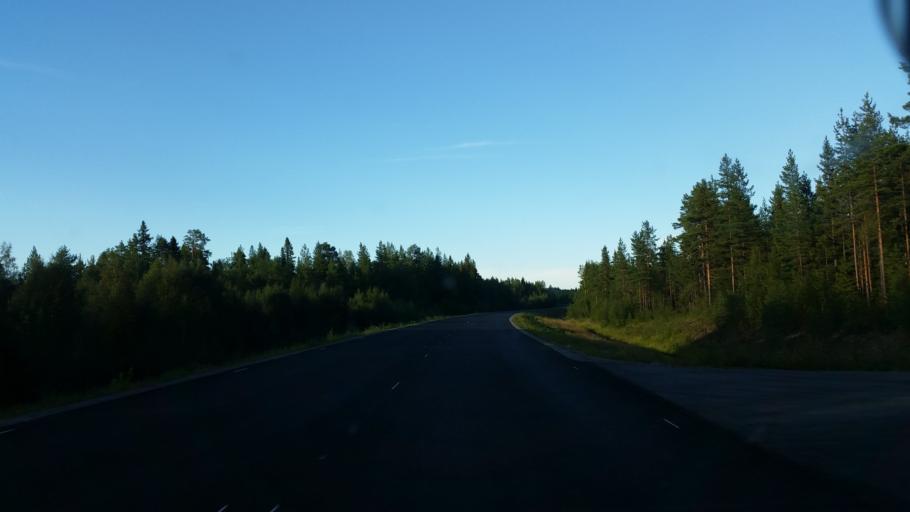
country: SE
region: Vaesterbotten
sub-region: Dorotea Kommun
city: Dorotea
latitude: 64.2869
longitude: 16.5120
